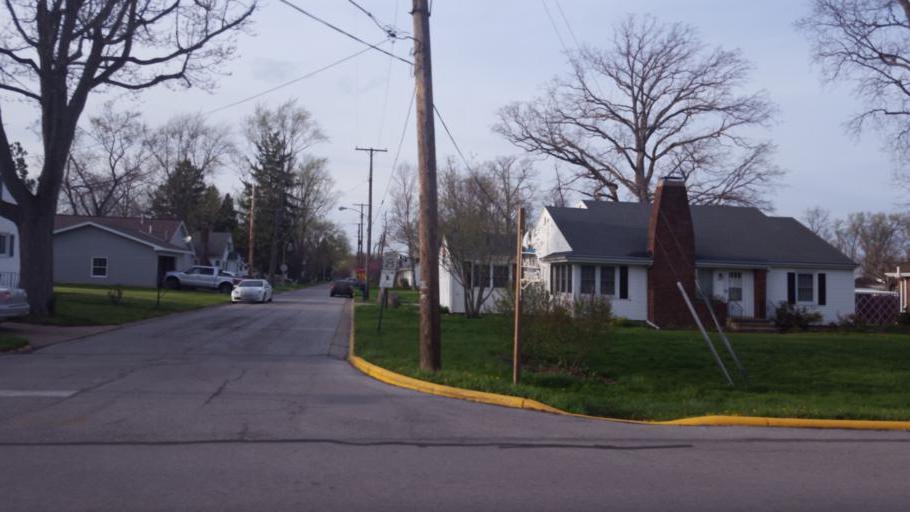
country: US
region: Ohio
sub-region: Erie County
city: Huron
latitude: 41.4085
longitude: -82.5859
